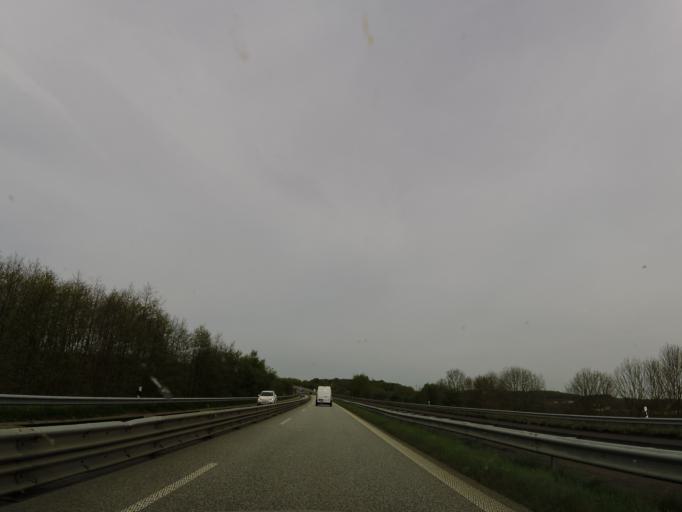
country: DE
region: Schleswig-Holstein
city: Arkebek
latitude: 54.1437
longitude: 9.2461
